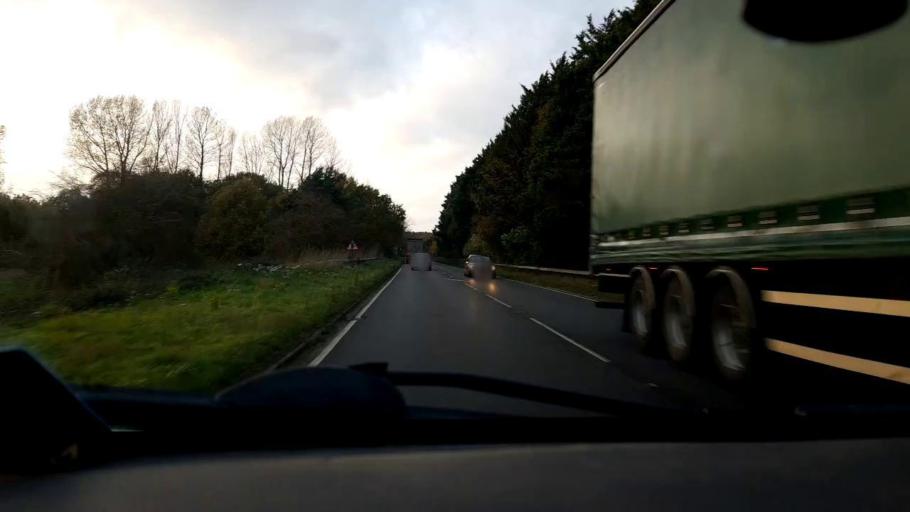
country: GB
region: England
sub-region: Norfolk
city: Costessey
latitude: 52.7057
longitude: 1.1516
